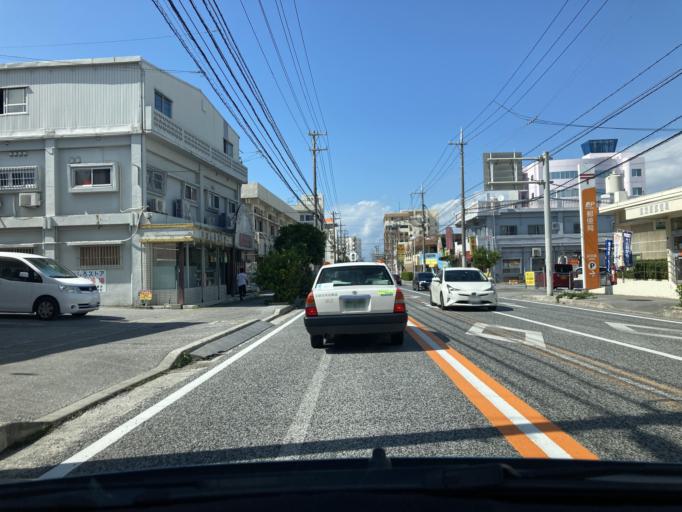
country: JP
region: Okinawa
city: Ginowan
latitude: 26.2612
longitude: 127.7431
